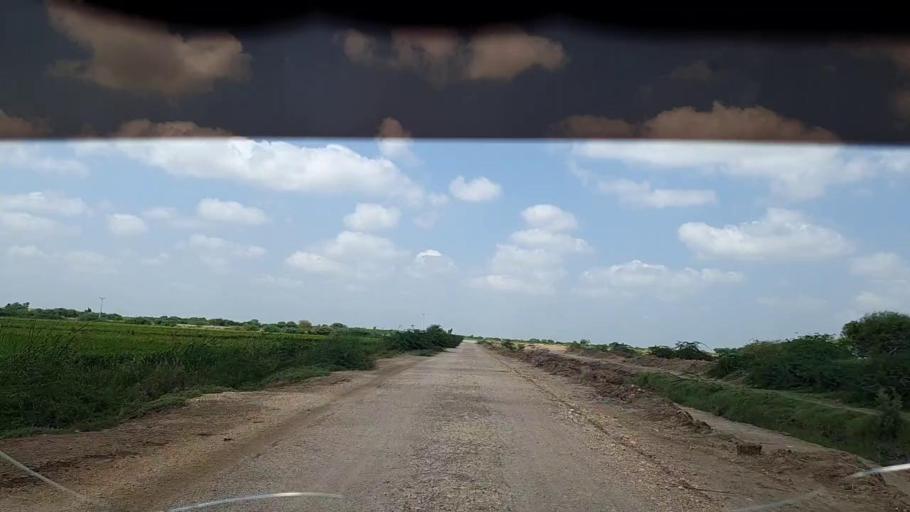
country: PK
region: Sindh
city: Kadhan
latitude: 24.5945
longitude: 68.9642
